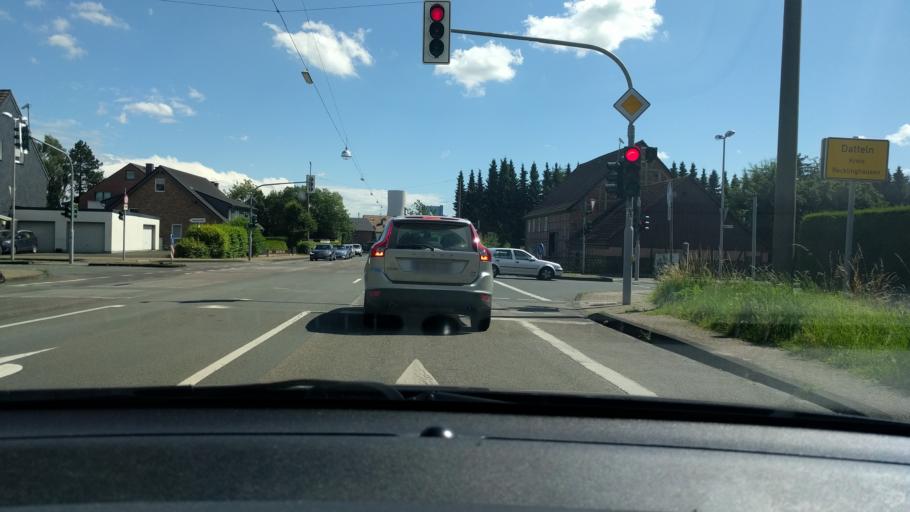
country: DE
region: North Rhine-Westphalia
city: Datteln
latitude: 51.6575
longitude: 7.3370
